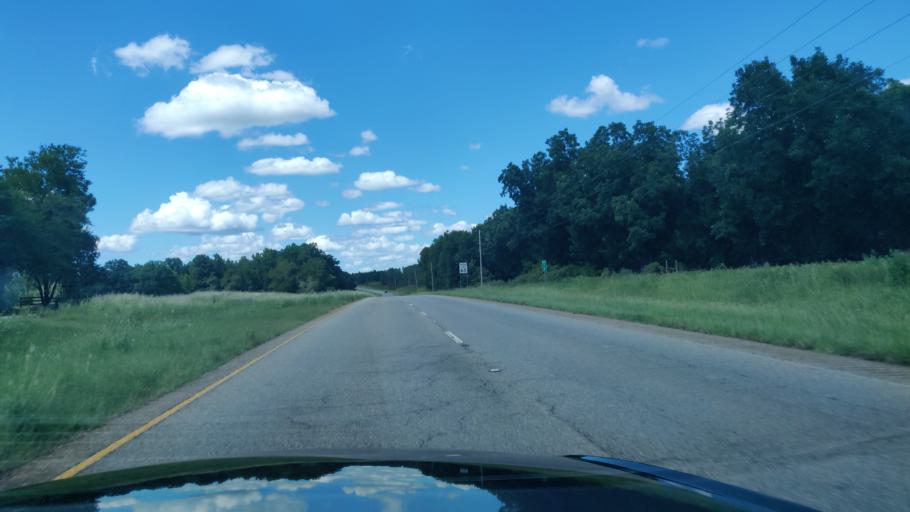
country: US
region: Georgia
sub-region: Stewart County
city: Richland
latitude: 32.0466
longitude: -84.6744
